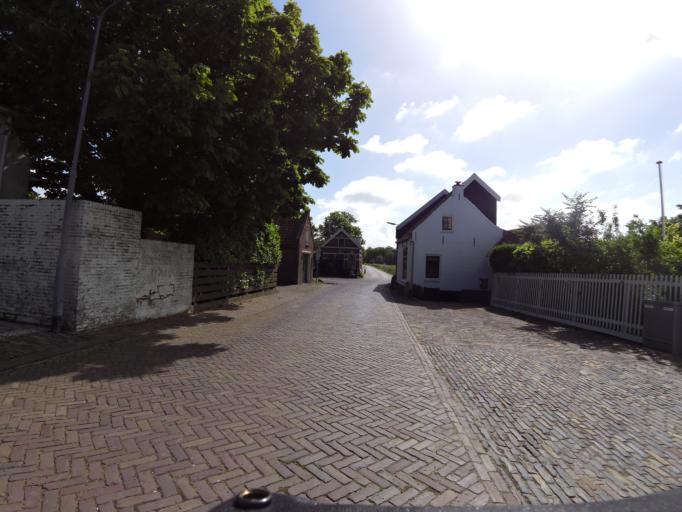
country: NL
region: Zeeland
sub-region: Schouwen-Duiveland
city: Scharendijke
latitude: 51.6934
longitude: 3.9392
